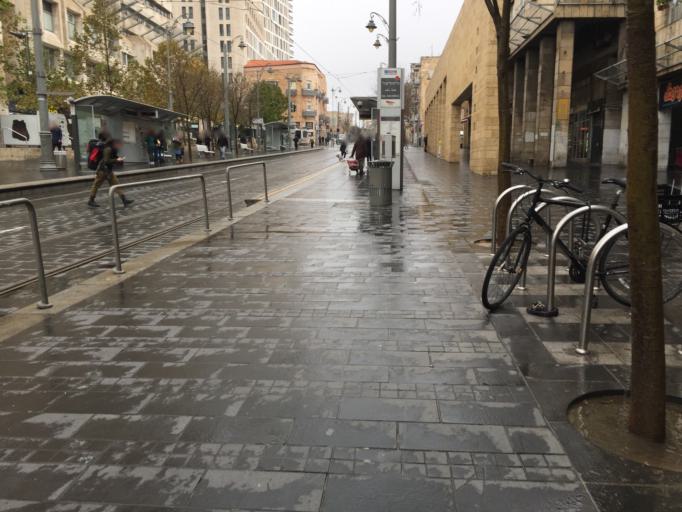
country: IL
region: Jerusalem
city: West Jerusalem
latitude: 31.7844
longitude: 35.2157
